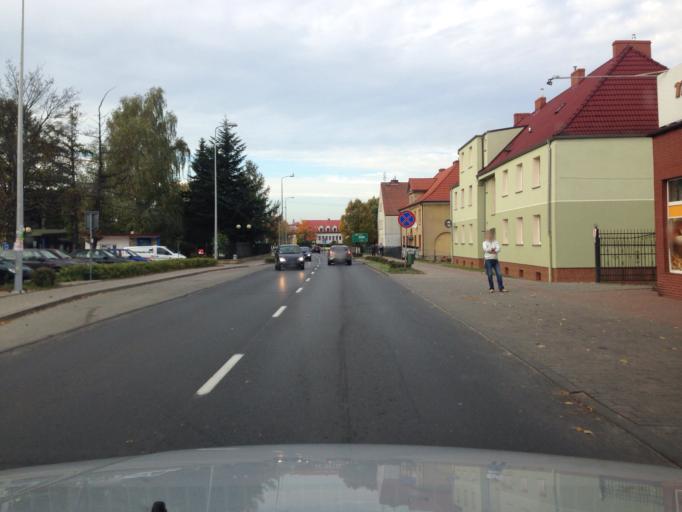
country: PL
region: Pomeranian Voivodeship
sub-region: Powiat leborski
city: Lebork
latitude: 54.5283
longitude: 17.7646
